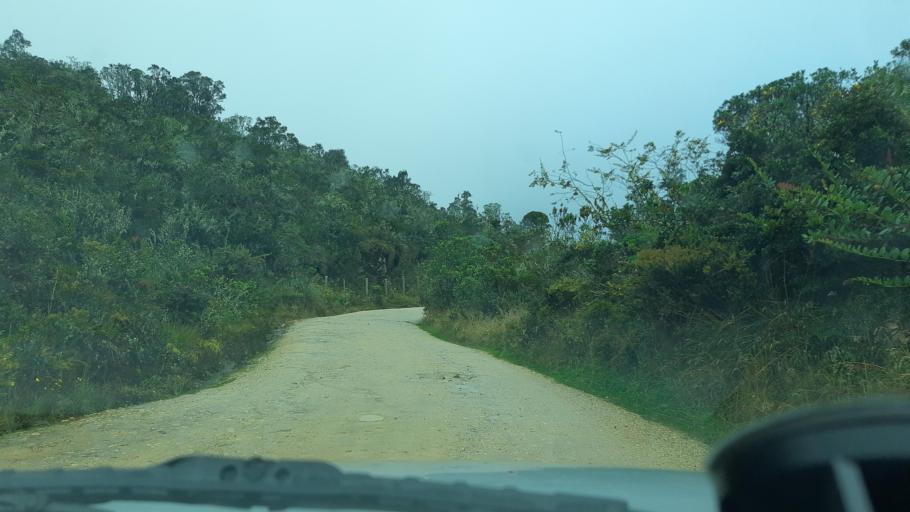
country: CO
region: Cundinamarca
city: Villapinzon
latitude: 5.2163
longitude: -73.5361
